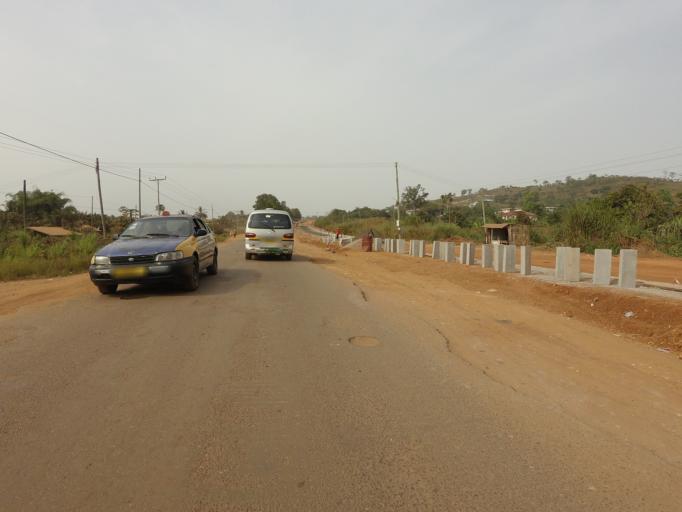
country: GH
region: Volta
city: Ho
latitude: 6.5957
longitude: 0.4426
